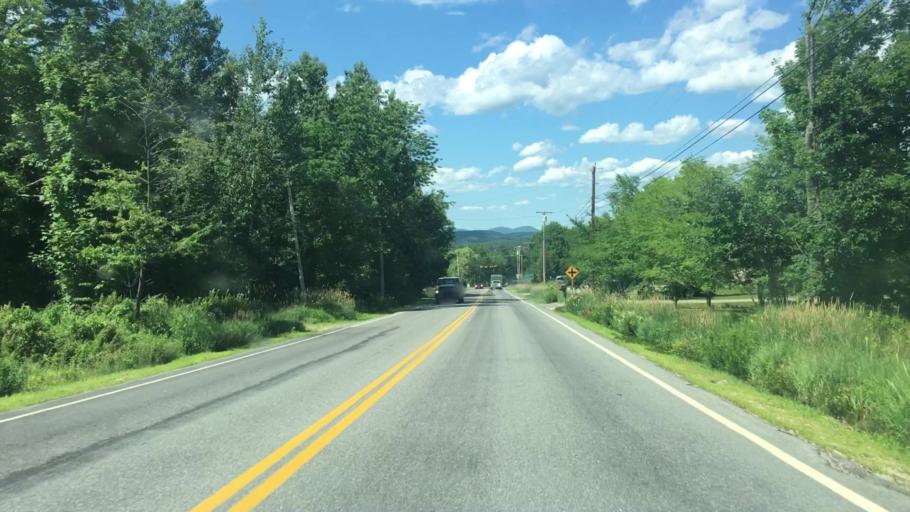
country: US
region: Maine
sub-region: Franklin County
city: Wilton
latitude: 44.5753
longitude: -70.1755
